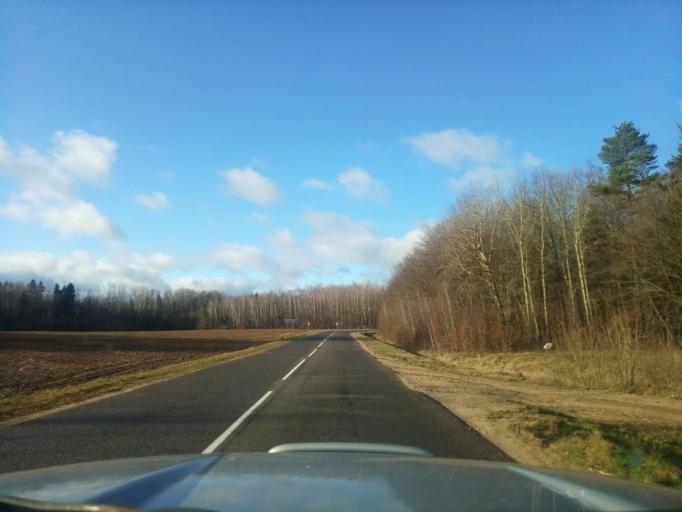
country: BY
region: Minsk
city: Kapyl'
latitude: 53.1713
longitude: 27.0285
